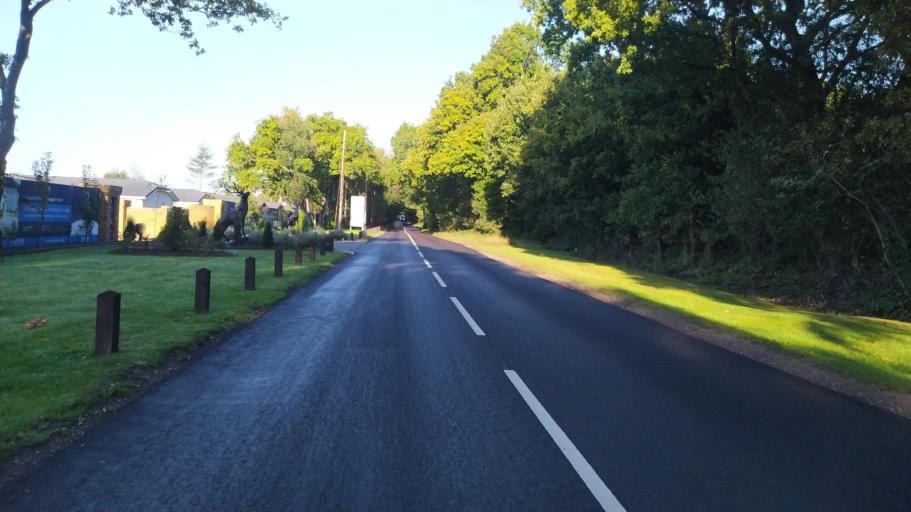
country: GB
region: England
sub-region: Dorset
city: Three Legged Cross
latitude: 50.8521
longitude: -1.8939
